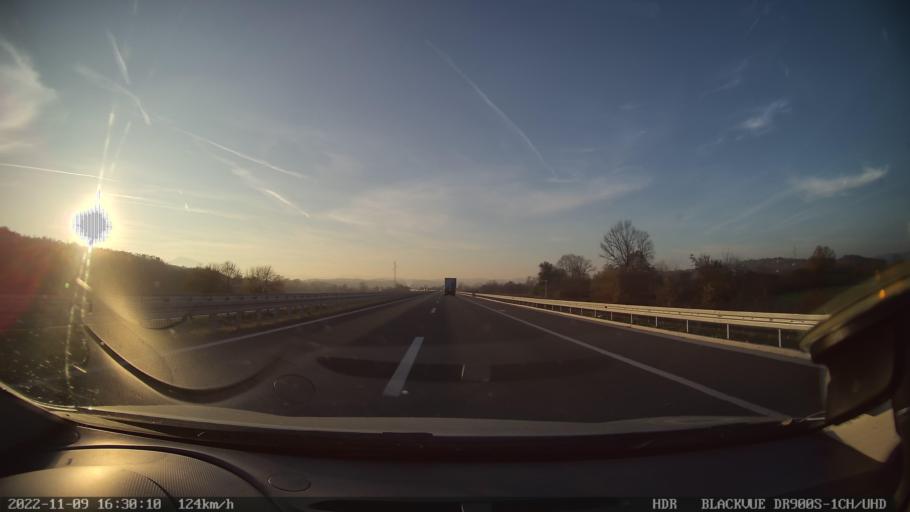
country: RS
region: Central Serbia
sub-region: Moravicki Okrug
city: Cacak
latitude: 43.9271
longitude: 20.3443
